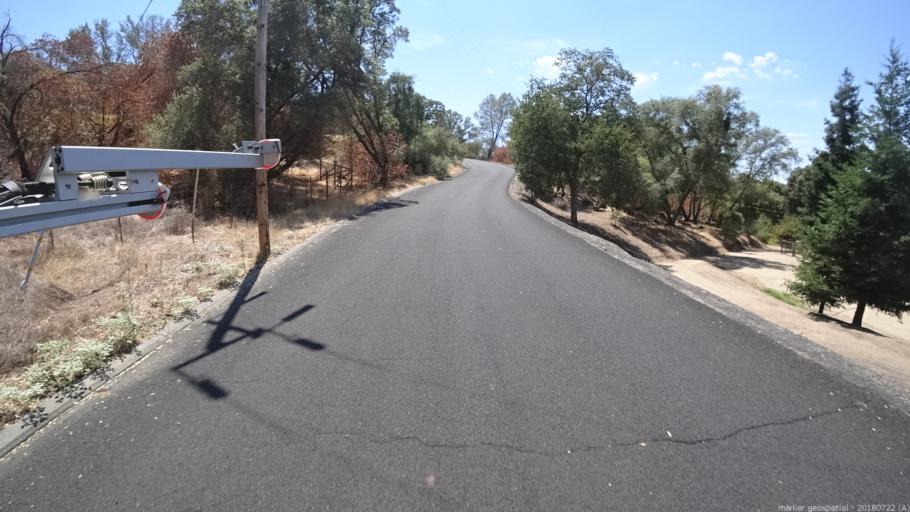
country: US
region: California
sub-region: Madera County
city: Yosemite Lakes
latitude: 37.2297
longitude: -119.7472
